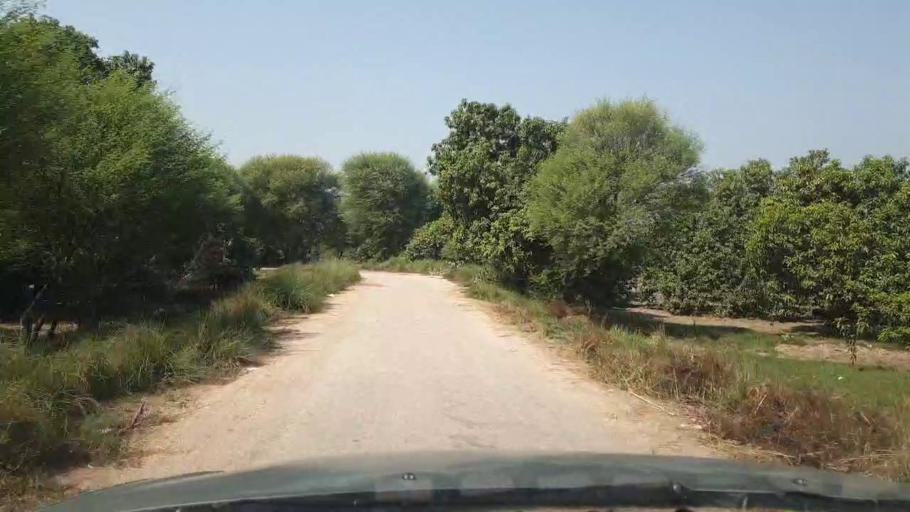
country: PK
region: Sindh
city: Tando Jam
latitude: 25.3642
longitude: 68.5254
